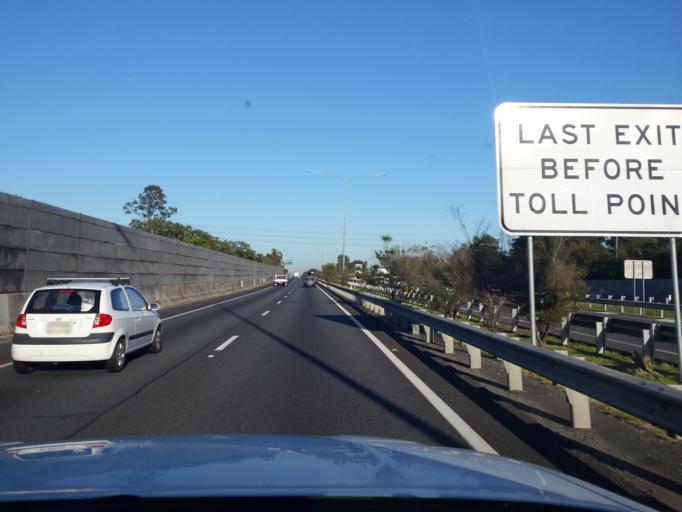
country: AU
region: Queensland
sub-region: Logan
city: Beenleigh
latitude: -27.6852
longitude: 153.1827
